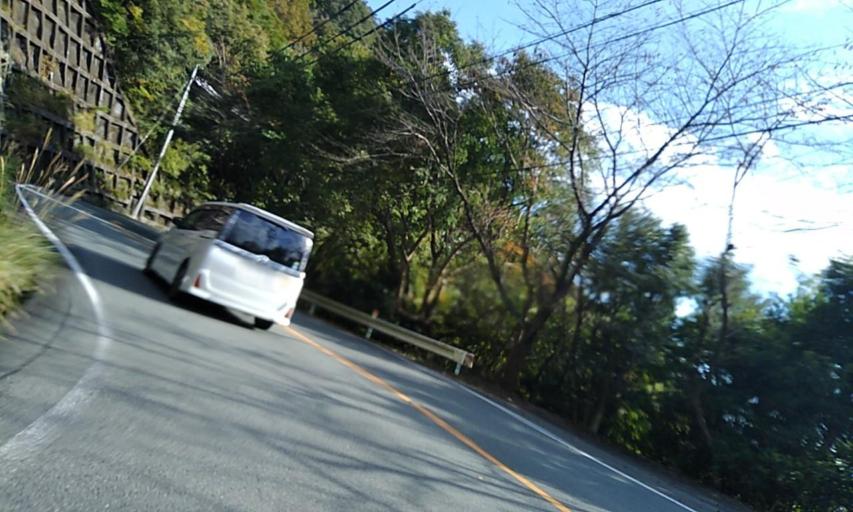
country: JP
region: Mie
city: Owase
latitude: 34.2208
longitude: 136.3925
